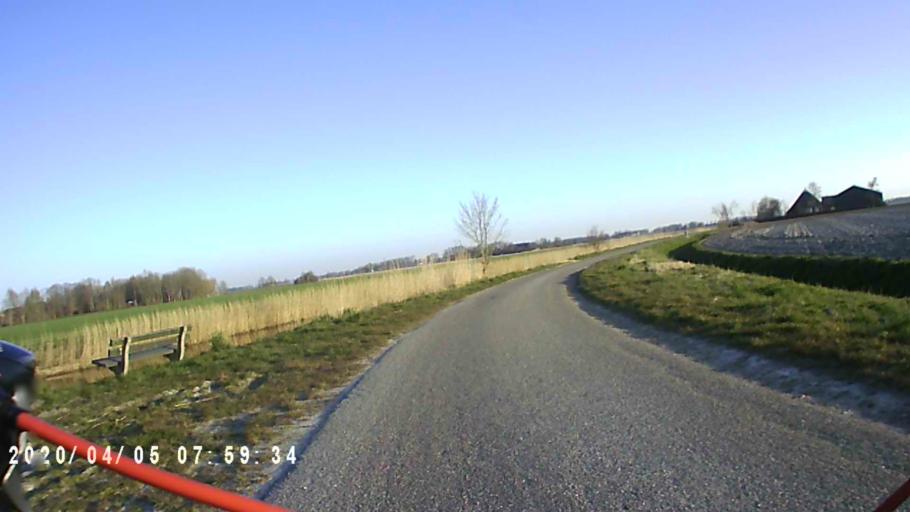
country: NL
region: Groningen
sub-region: Gemeente Zuidhorn
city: Oldehove
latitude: 53.3406
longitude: 6.4311
